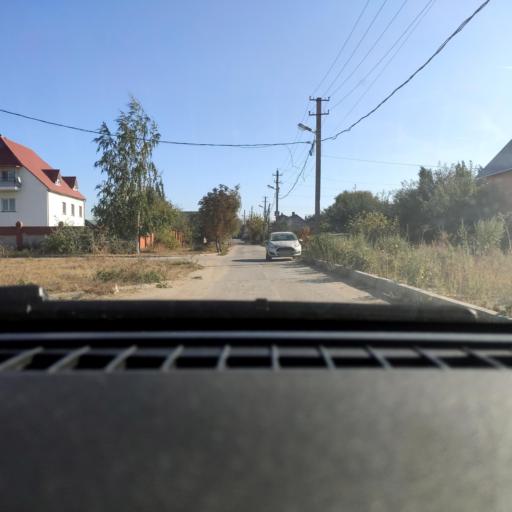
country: RU
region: Voronezj
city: Voronezh
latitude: 51.6681
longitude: 39.2797
